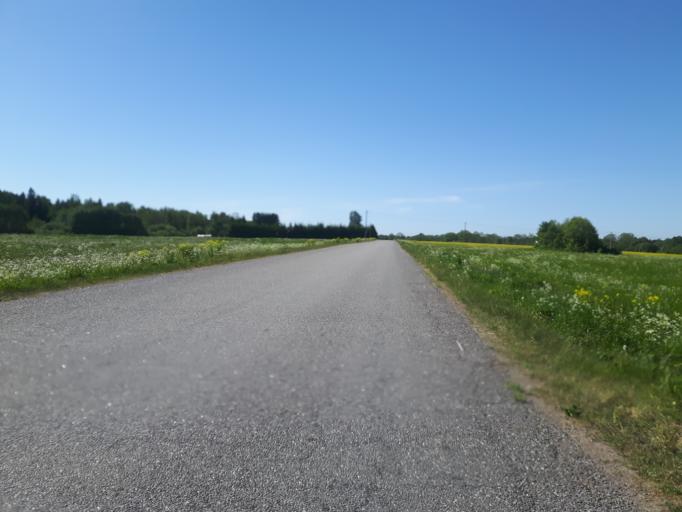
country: EE
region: Laeaene-Virumaa
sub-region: Haljala vald
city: Haljala
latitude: 59.5421
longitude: 26.2222
